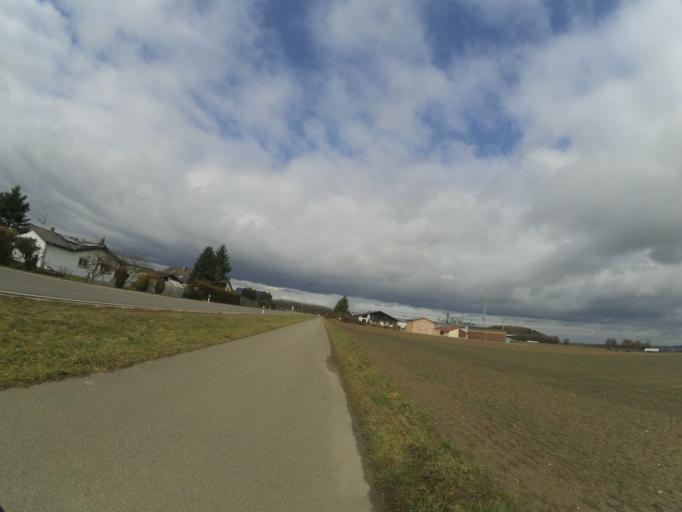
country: DE
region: Bavaria
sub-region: Swabia
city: Vohringen
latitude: 48.2971
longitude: 10.1062
